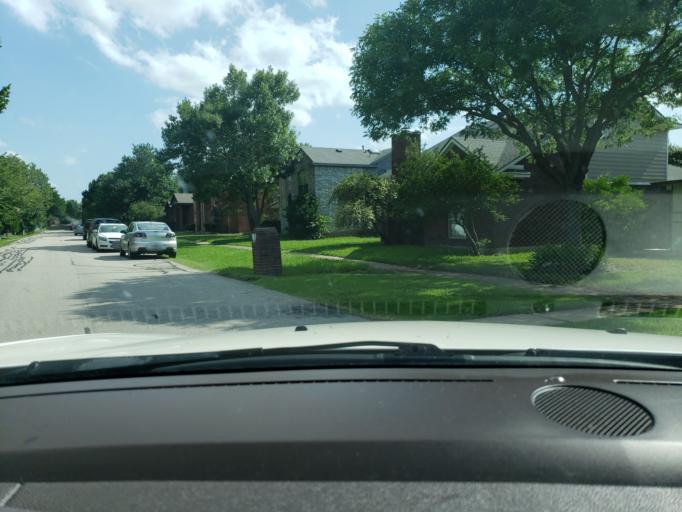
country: US
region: Texas
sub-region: Dallas County
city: Rowlett
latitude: 32.8961
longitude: -96.5742
